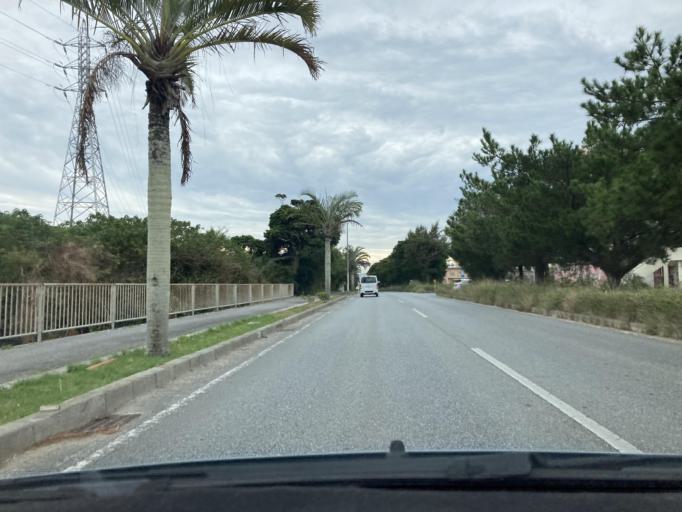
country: JP
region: Okinawa
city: Okinawa
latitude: 26.3888
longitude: 127.7549
